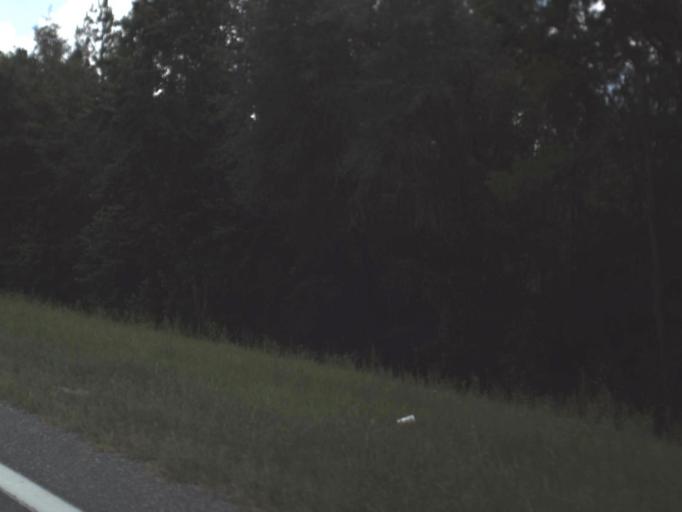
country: US
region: Florida
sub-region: Suwannee County
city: Wellborn
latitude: 30.3201
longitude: -82.7811
